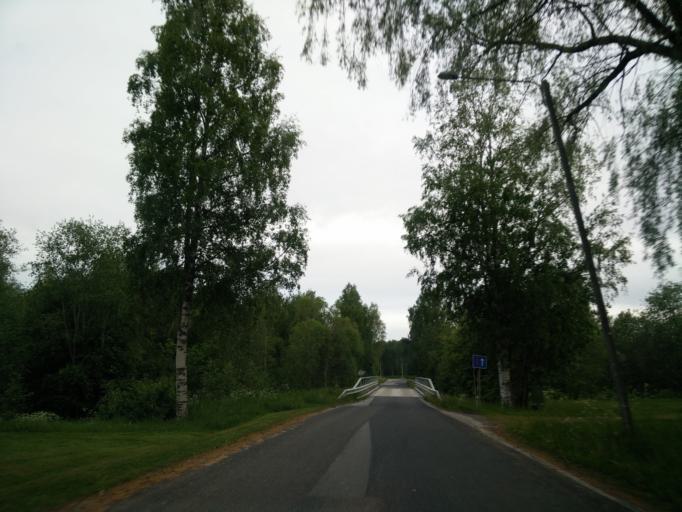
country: SE
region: Vaesternorrland
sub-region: Kramfors Kommun
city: Kramfors
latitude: 63.0479
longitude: 17.8005
